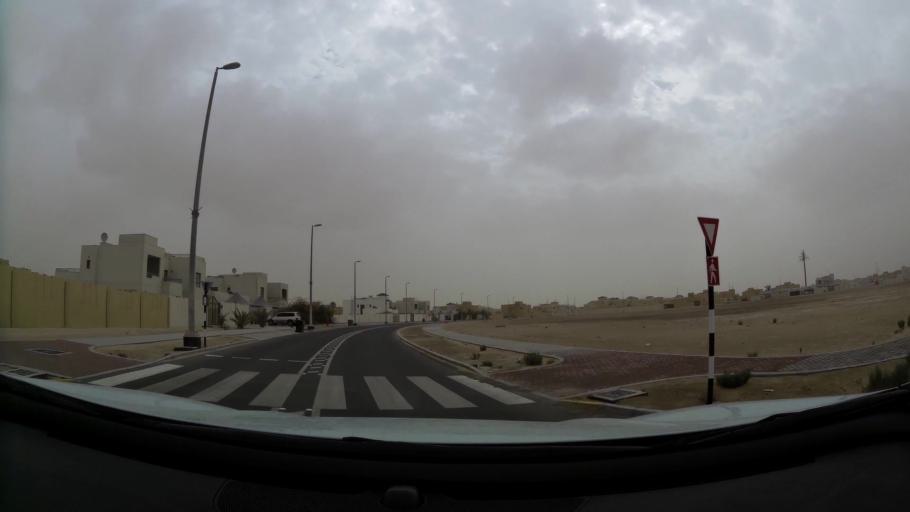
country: AE
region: Abu Dhabi
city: Abu Dhabi
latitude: 24.4543
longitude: 54.7347
